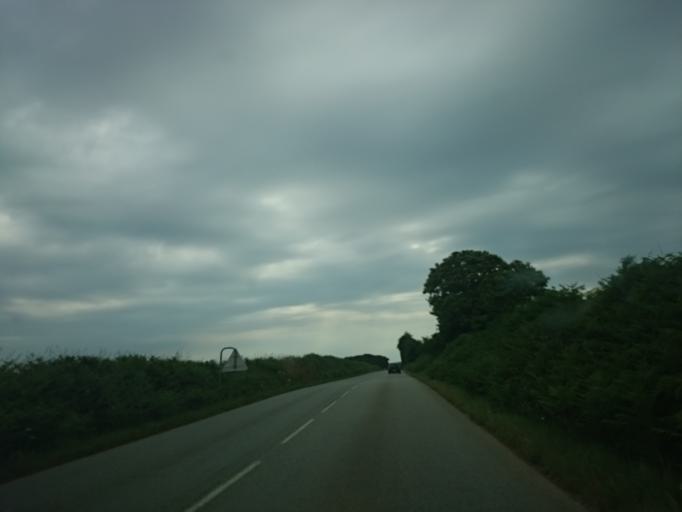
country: FR
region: Brittany
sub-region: Departement du Finistere
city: Ploumoguer
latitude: 48.3894
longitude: -4.6833
